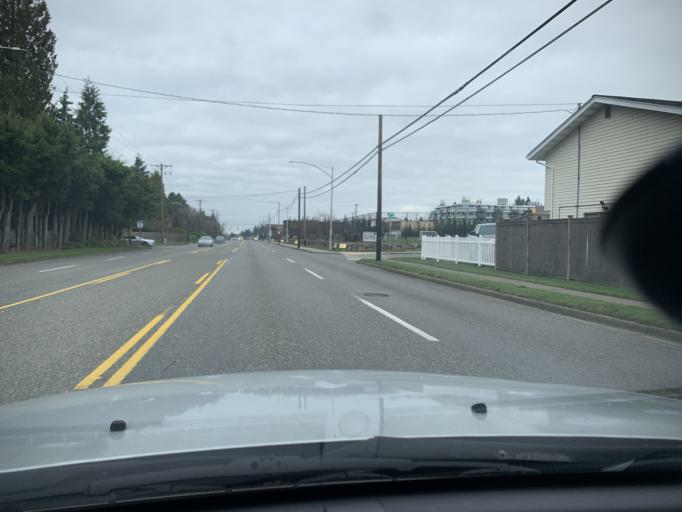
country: US
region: Washington
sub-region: Pierce County
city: University Place
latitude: 47.2532
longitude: -122.5369
